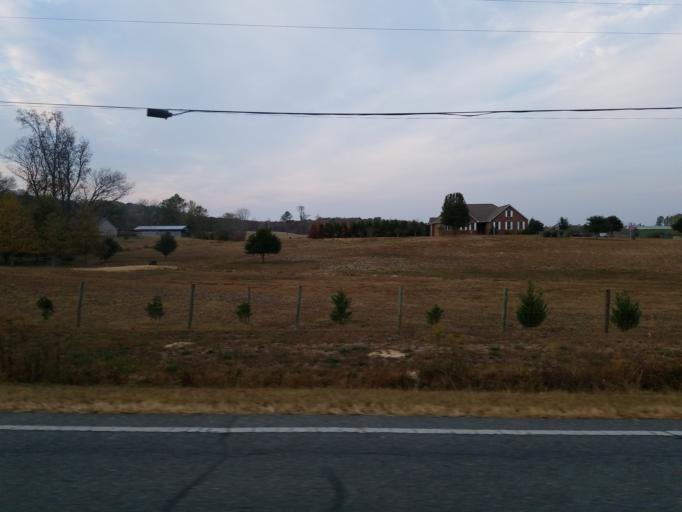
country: US
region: Georgia
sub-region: Gordon County
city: Calhoun
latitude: 34.6018
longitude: -84.8391
